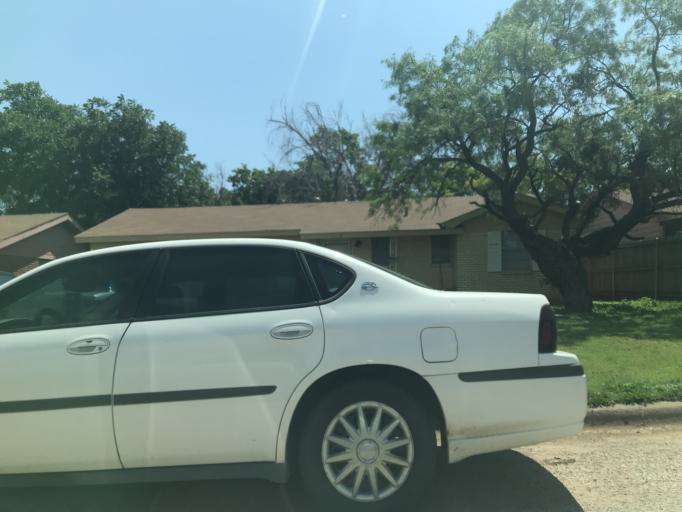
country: US
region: Texas
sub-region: Taylor County
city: Abilene
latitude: 32.4748
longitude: -99.7674
